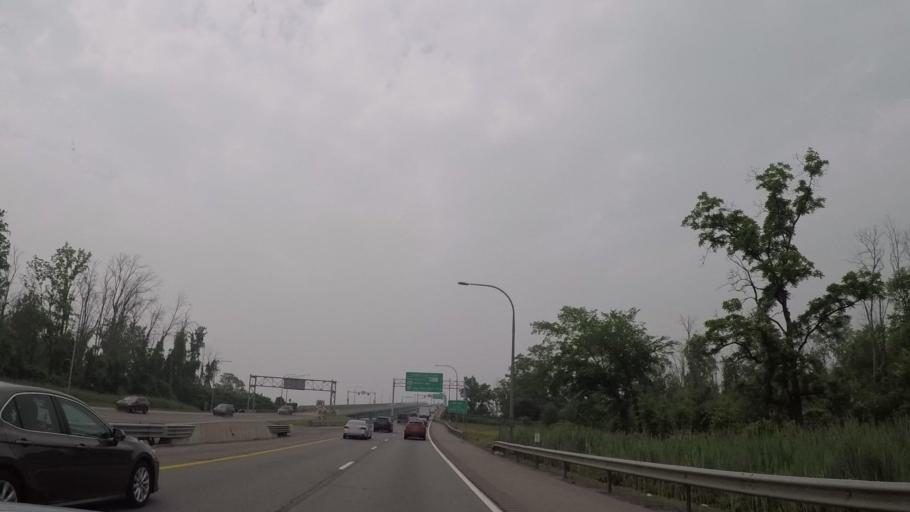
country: US
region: New York
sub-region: Niagara County
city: Niagara Falls
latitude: 43.0620
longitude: -78.9905
